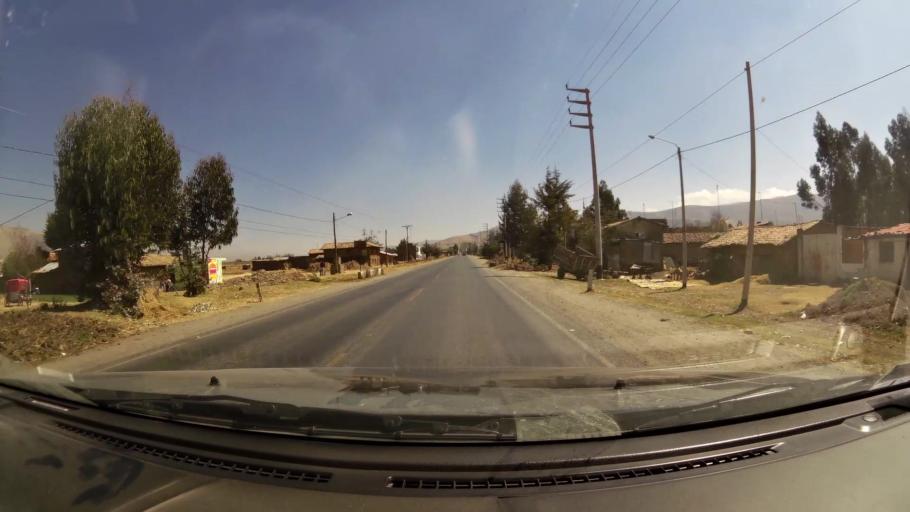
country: PE
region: Junin
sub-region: Provincia de Jauja
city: San Lorenzo
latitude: -11.8410
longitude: -75.3902
